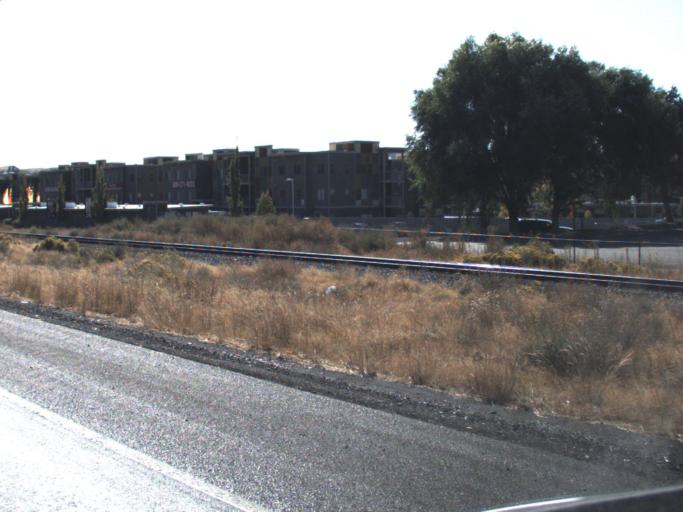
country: US
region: Washington
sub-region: Benton County
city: Richland
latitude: 46.2662
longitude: -119.2997
